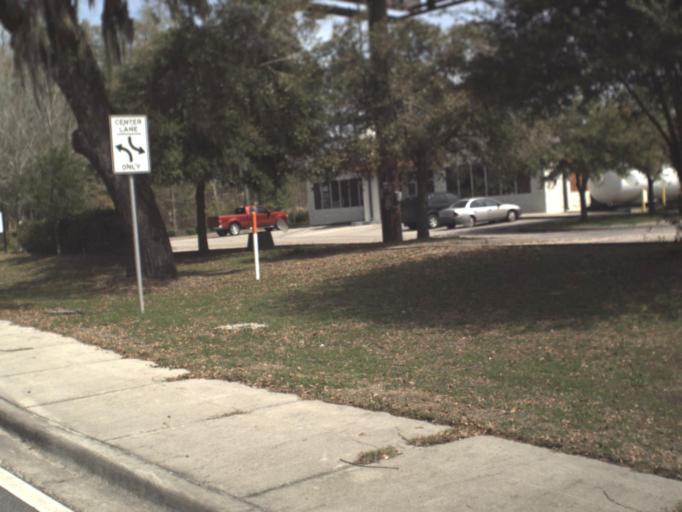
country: US
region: Florida
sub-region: Gadsden County
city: Midway
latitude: 30.5156
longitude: -84.3665
